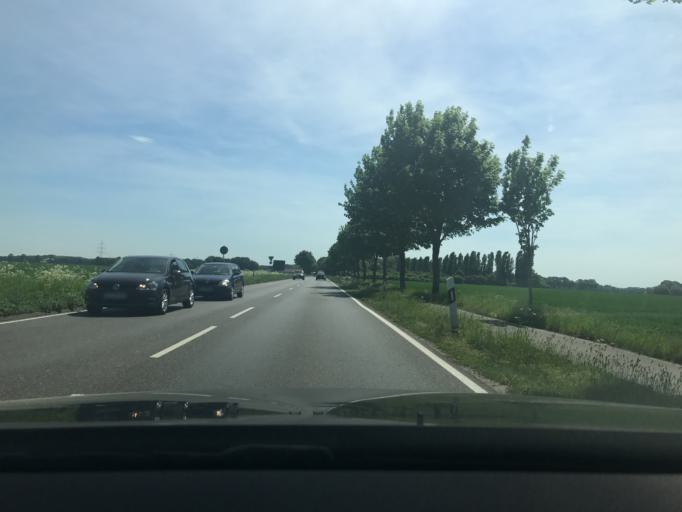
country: DE
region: North Rhine-Westphalia
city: Tonisvorst
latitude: 51.3124
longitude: 6.4781
